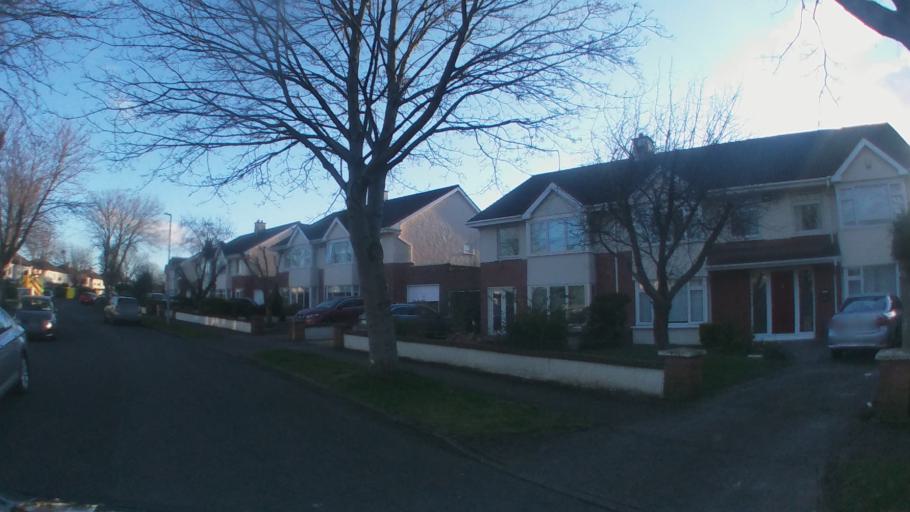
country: IE
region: Leinster
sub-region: Fingal County
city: Blanchardstown
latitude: 53.3771
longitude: -6.3866
